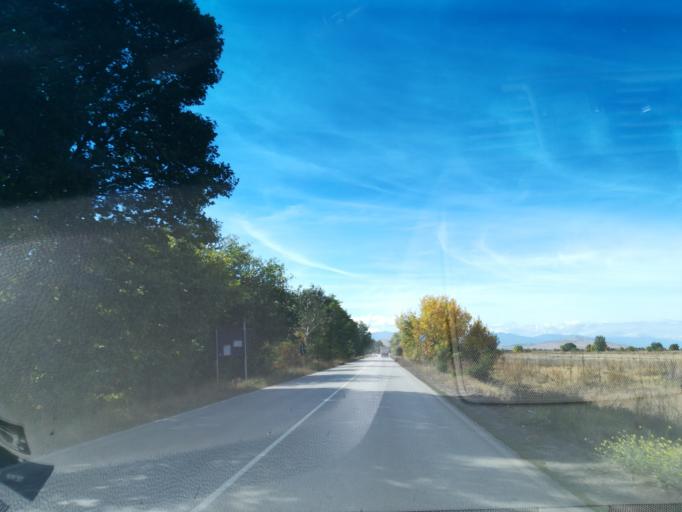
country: BG
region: Plovdiv
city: Stamboliyski
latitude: 42.1197
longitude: 24.5509
